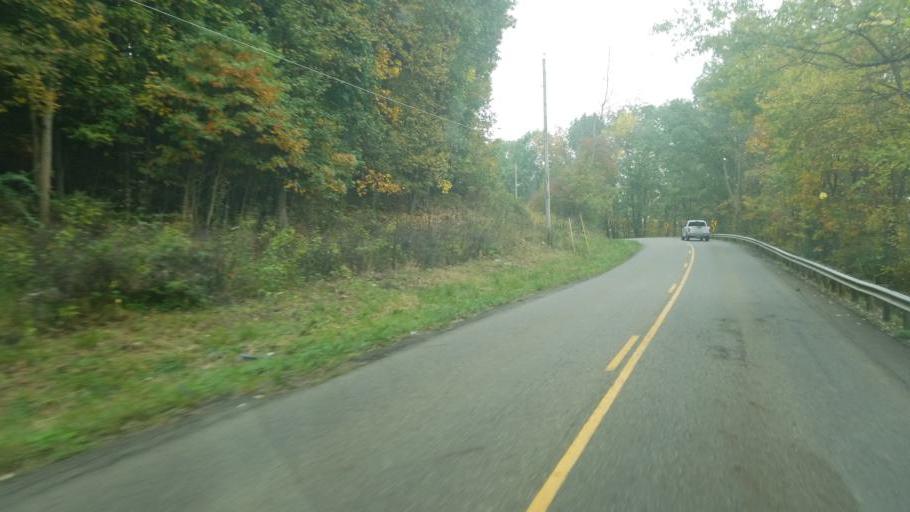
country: US
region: Ohio
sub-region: Tuscarawas County
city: Strasburg
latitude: 40.6380
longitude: -81.3981
